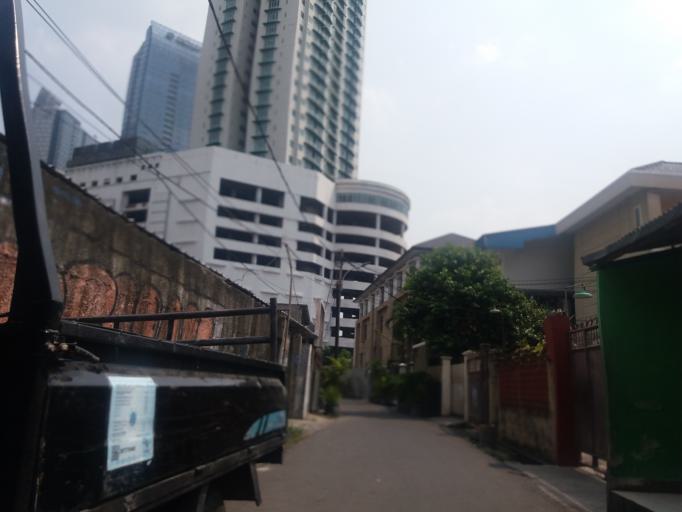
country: ID
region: Jakarta Raya
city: Jakarta
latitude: -6.2226
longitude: 106.8274
